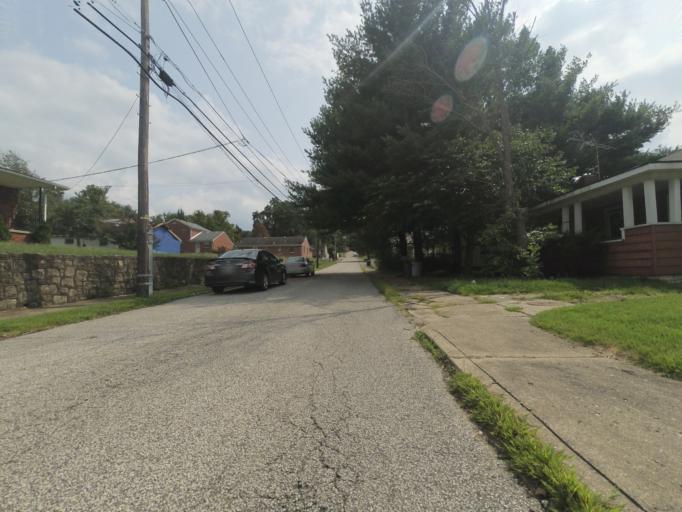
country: US
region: West Virginia
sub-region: Cabell County
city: Huntington
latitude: 38.4016
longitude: -82.4061
